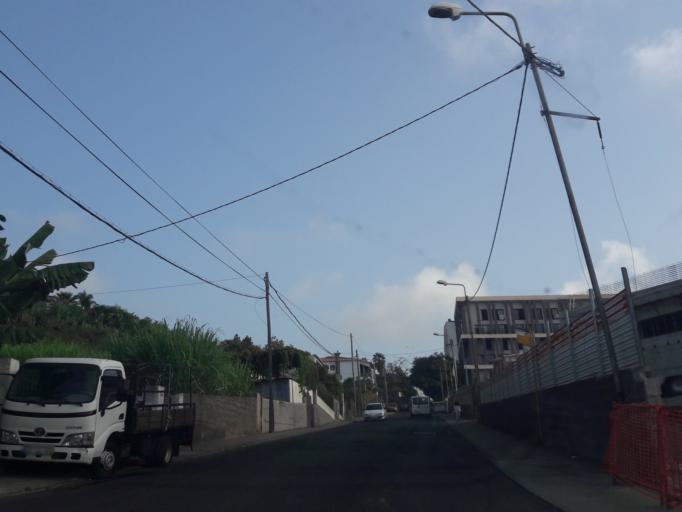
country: PT
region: Madeira
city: Camara de Lobos
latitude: 32.6475
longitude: -16.9423
